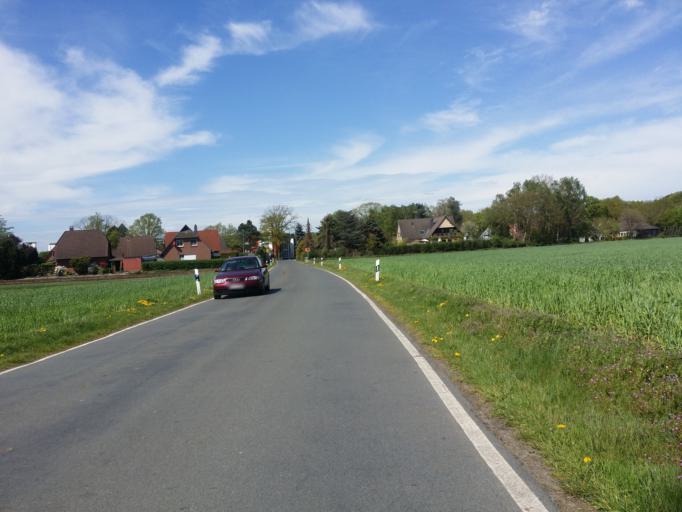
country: DE
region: Lower Saxony
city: Delmenhorst
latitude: 53.0783
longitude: 8.6484
